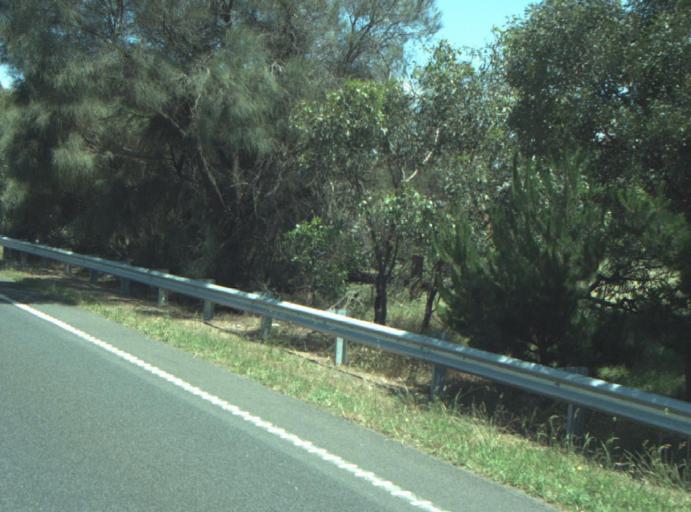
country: AU
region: Victoria
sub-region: Queenscliffe
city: Queenscliff
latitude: -38.1814
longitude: 144.6921
